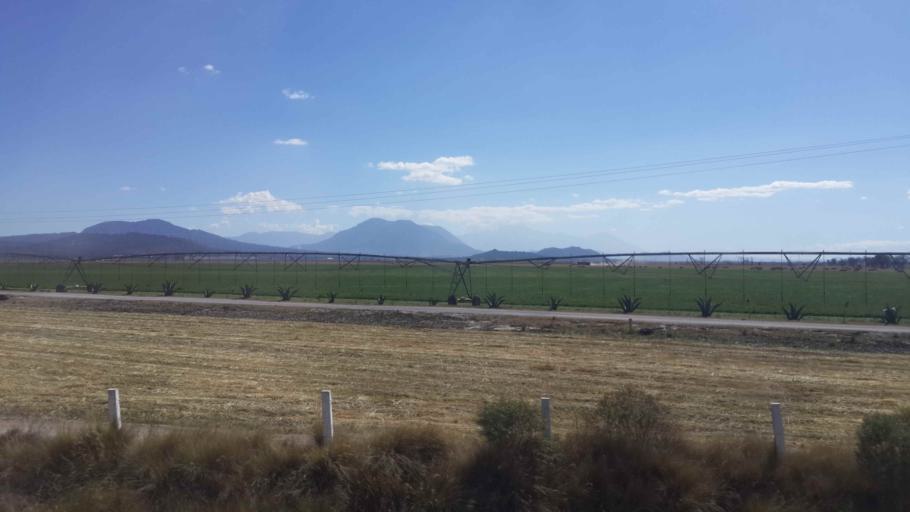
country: MX
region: Puebla
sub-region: Oriental
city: San Antonio Virreyes
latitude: 19.4281
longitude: -97.6277
